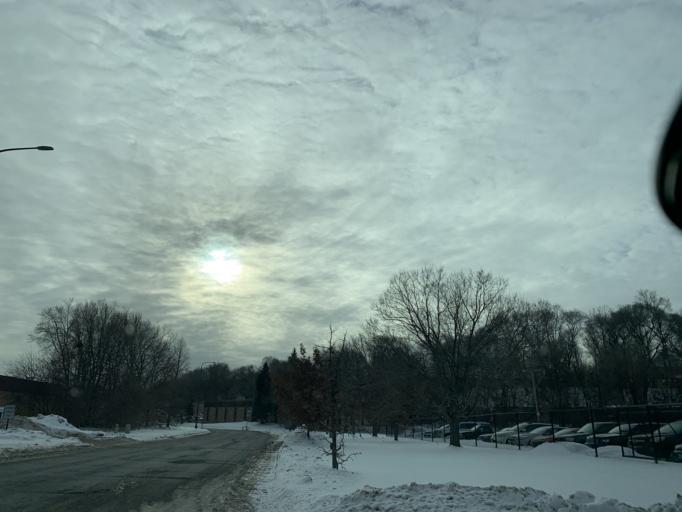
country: US
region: Minnesota
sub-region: Ramsey County
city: Saint Paul
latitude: 44.9365
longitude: -93.0791
